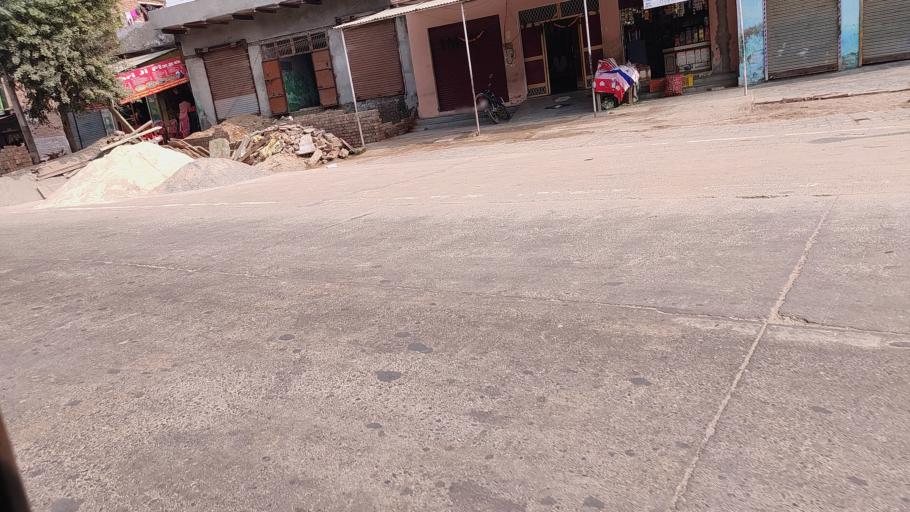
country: IN
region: Uttar Pradesh
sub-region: Mathura
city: Barsana
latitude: 27.6551
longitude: 77.3820
